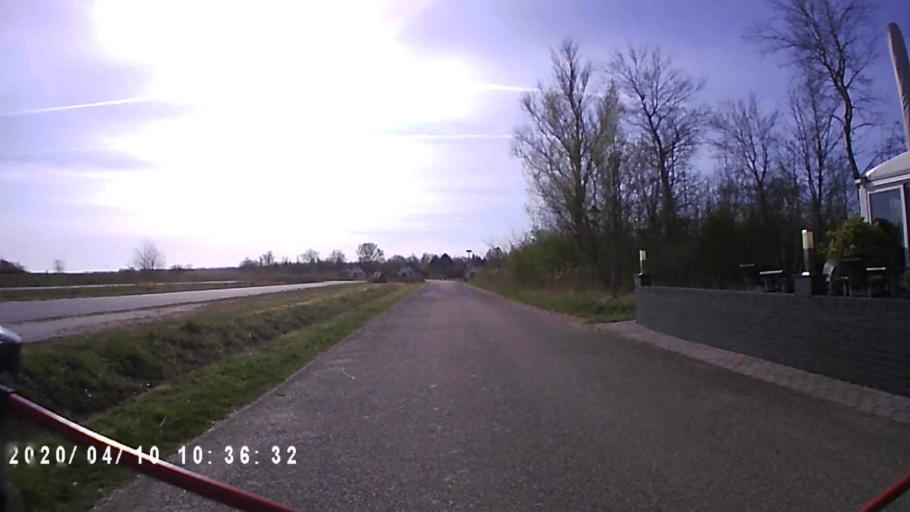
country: NL
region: Friesland
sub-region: Gemeente Dongeradeel
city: Anjum
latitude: 53.3906
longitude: 6.2150
